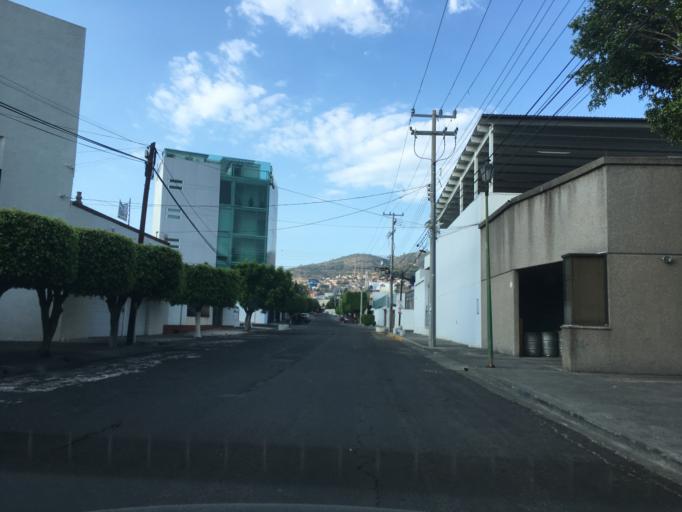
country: MX
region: Michoacan
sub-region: Morelia
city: Puerto de Buenavista (Lazaro Cardenas)
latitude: 19.6886
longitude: -101.1531
